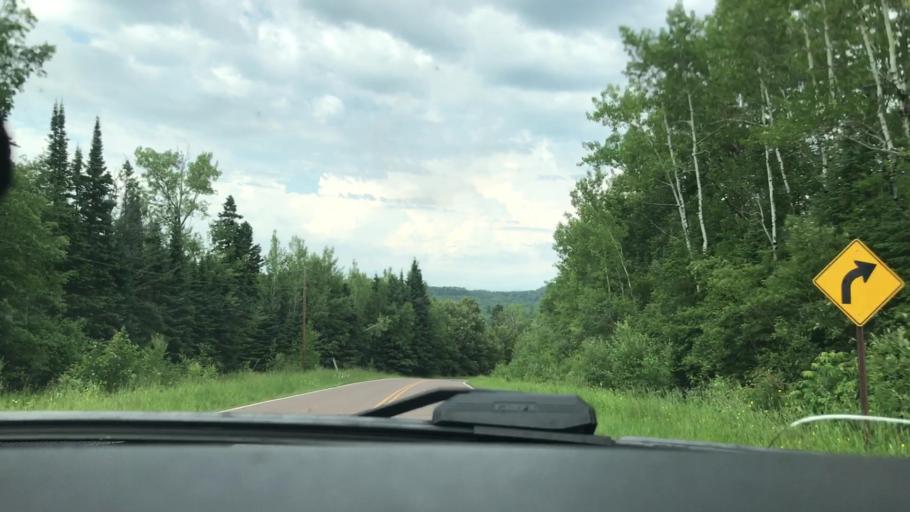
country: CA
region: Ontario
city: Neebing
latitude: 47.9634
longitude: -89.6914
